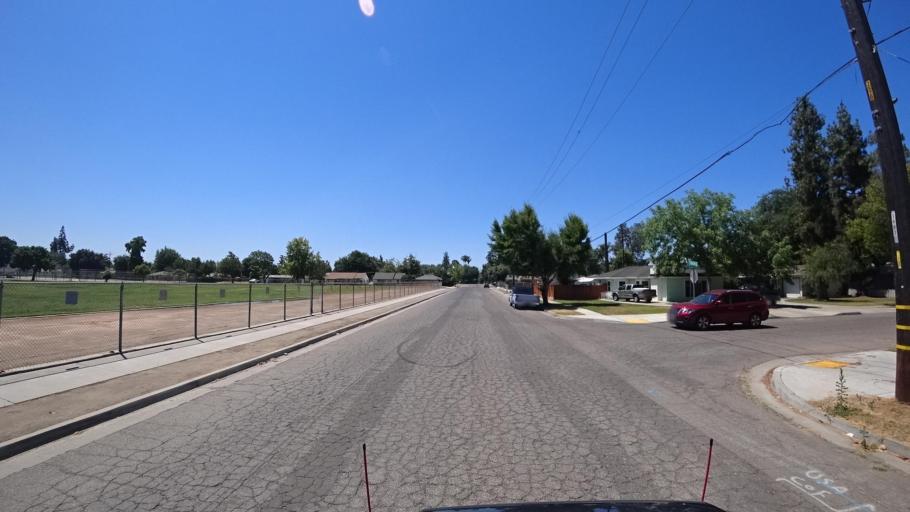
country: US
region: California
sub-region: Fresno County
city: Fresno
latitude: 36.7860
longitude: -119.7973
